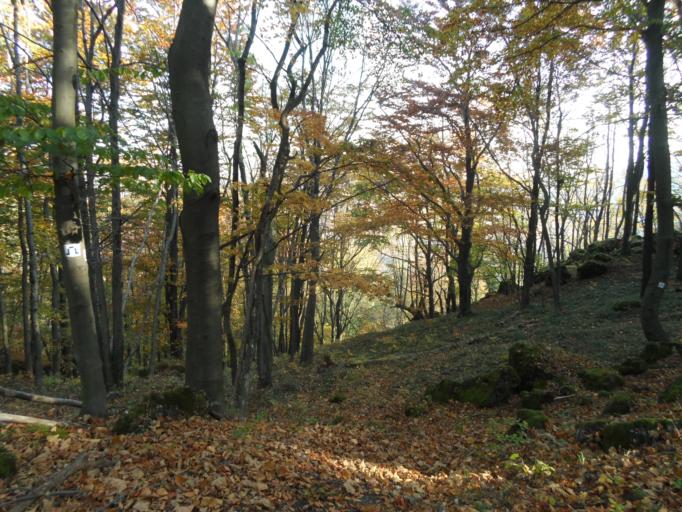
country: HU
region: Veszprem
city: Herend
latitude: 47.2321
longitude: 17.6711
